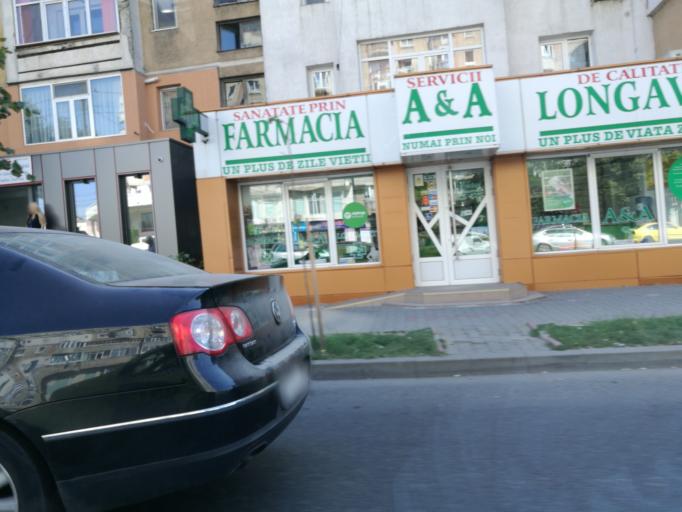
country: RO
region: Iasi
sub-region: Municipiul Iasi
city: Iasi
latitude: 47.1670
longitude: 27.5693
